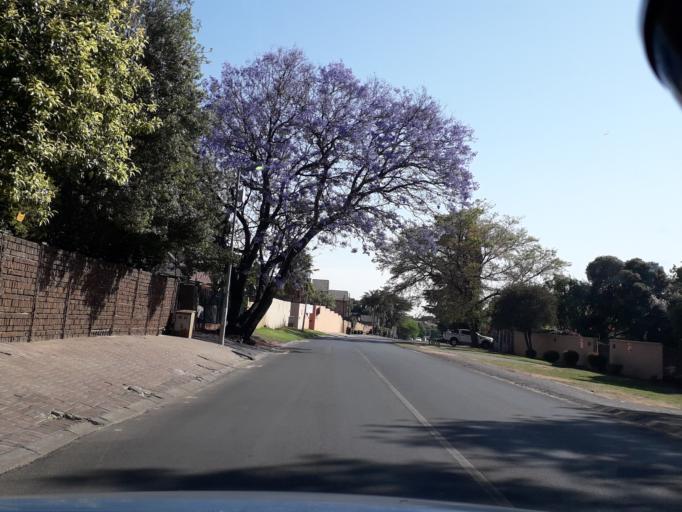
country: ZA
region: Gauteng
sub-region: City of Johannesburg Metropolitan Municipality
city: Roodepoort
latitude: -26.0904
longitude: 27.9316
